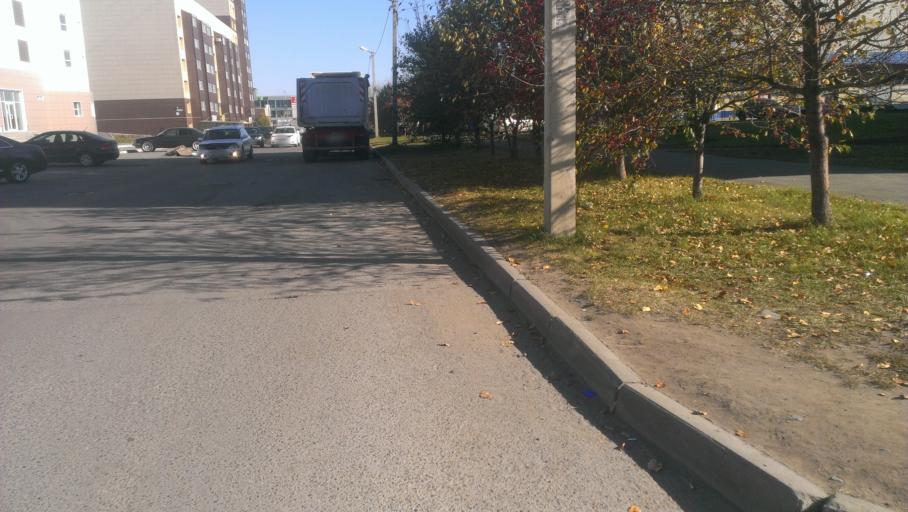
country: RU
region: Altai Krai
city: Novosilikatnyy
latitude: 53.3294
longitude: 83.6889
